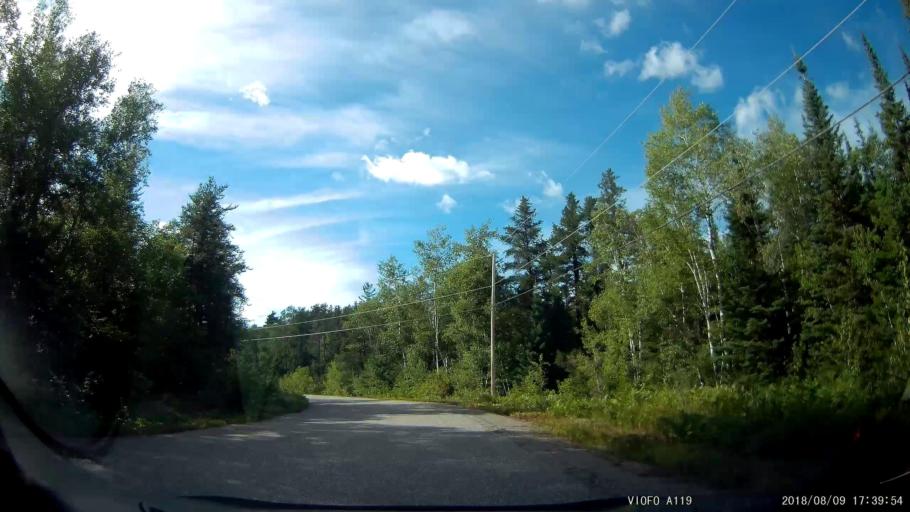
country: CA
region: Ontario
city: Rayside-Balfour
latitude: 46.6056
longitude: -81.4974
